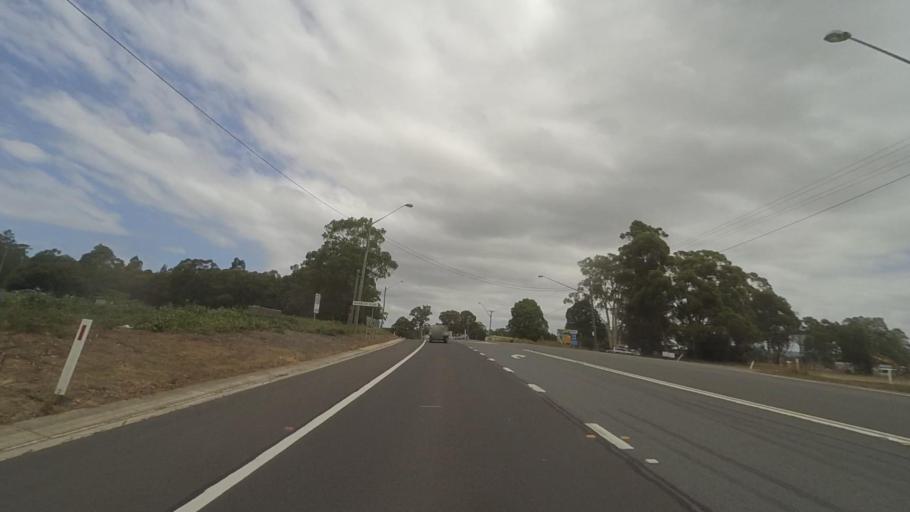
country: AU
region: New South Wales
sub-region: Shoalhaven Shire
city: Falls Creek
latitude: -35.0885
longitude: 150.5108
